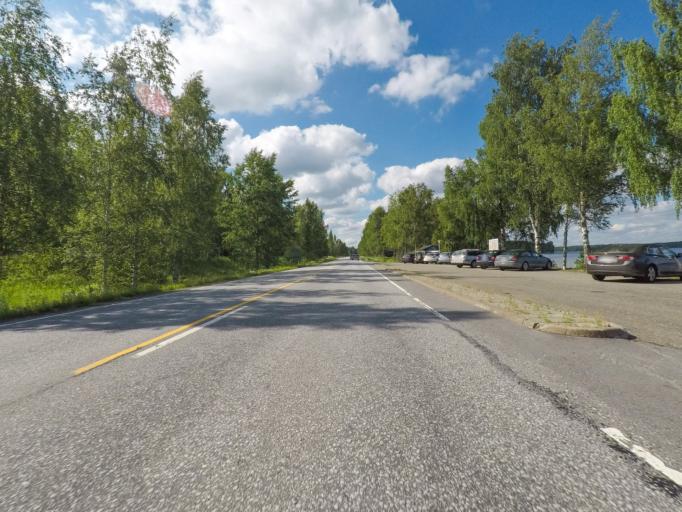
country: FI
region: Southern Savonia
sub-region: Savonlinna
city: Kerimaeki
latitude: 61.8071
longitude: 29.2774
